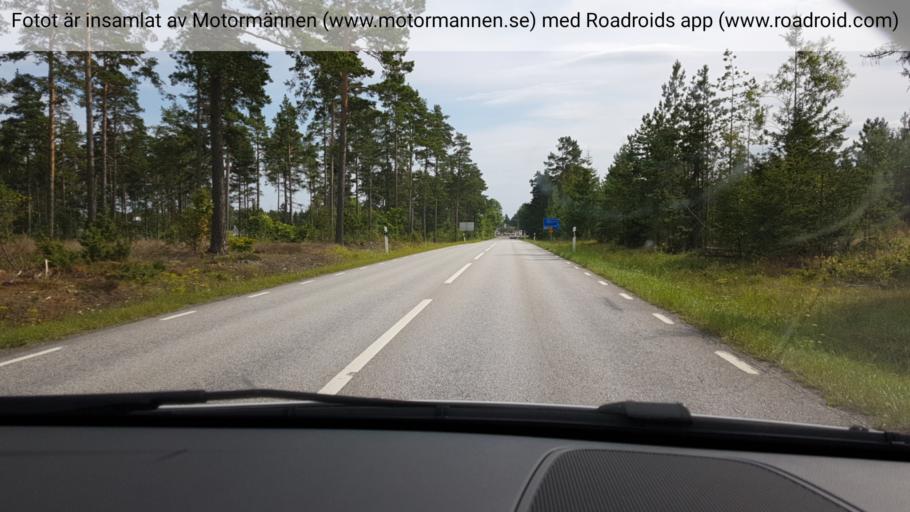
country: SE
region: Uppsala
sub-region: Osthammars Kommun
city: OEsthammar
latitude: 60.2585
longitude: 18.3417
